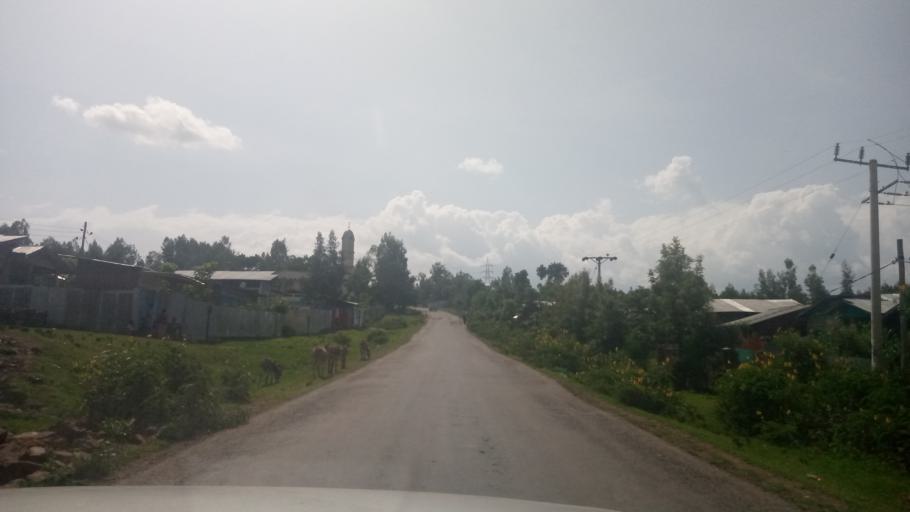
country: ET
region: Oromiya
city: Agaro
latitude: 7.9989
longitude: 36.4989
